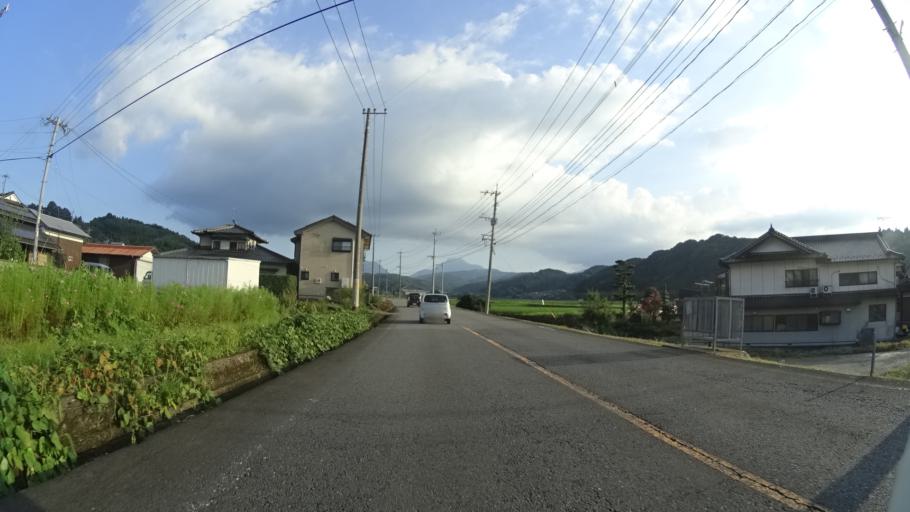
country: JP
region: Oita
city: Hiji
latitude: 33.4039
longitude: 131.3868
